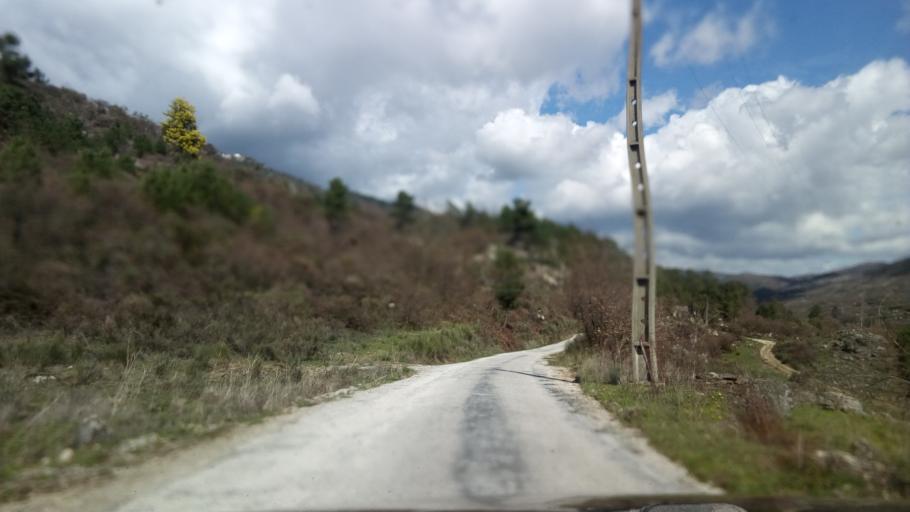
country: PT
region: Guarda
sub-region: Fornos de Algodres
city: Fornos de Algodres
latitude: 40.6348
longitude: -7.5153
